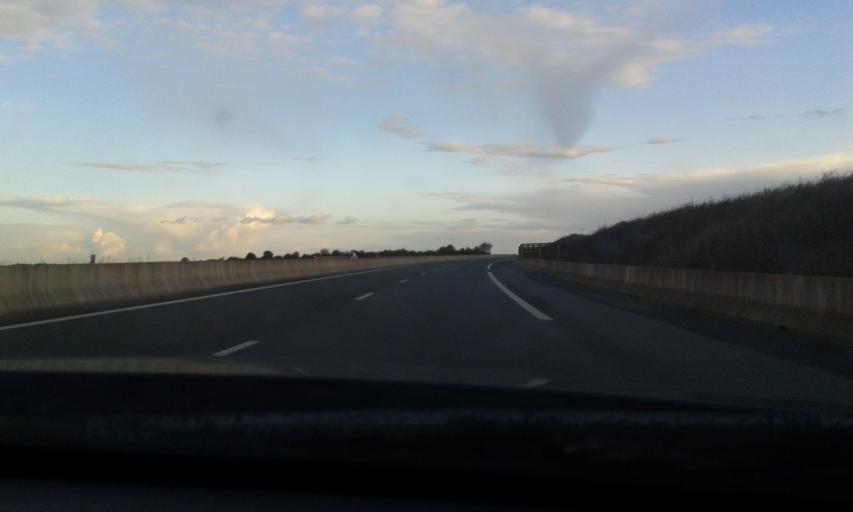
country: FR
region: Centre
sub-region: Departement d'Eure-et-Loir
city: Voves
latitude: 48.2694
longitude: 1.7541
